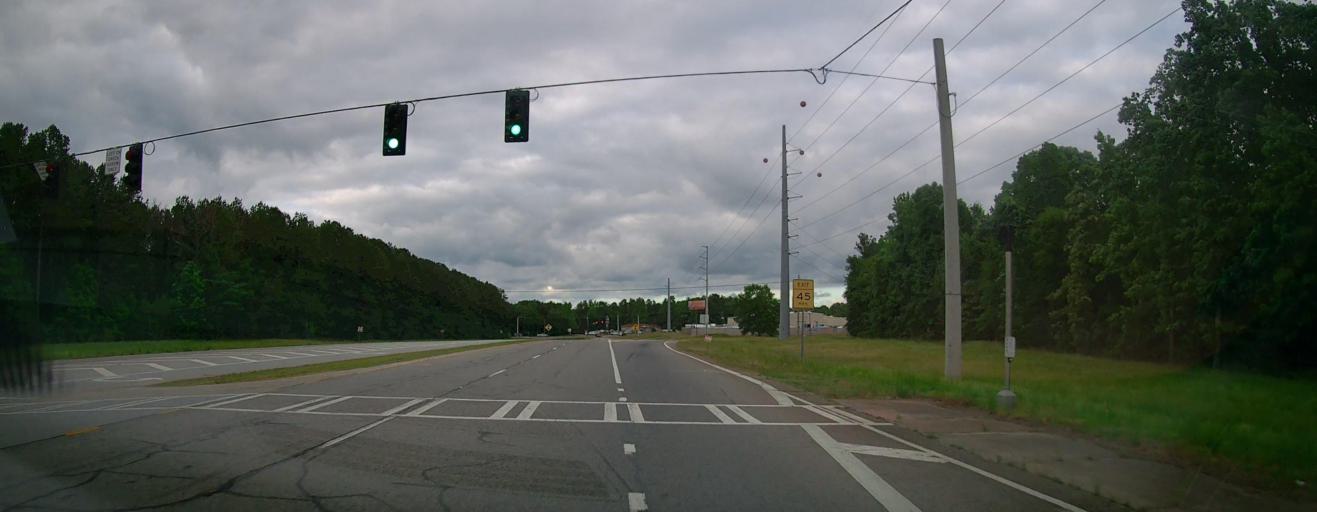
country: US
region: Georgia
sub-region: Oconee County
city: Bogart
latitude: 33.9385
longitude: -83.5039
